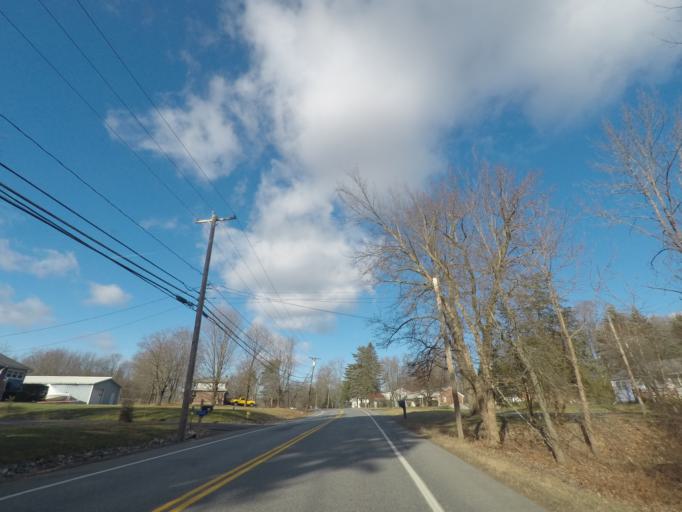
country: US
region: New York
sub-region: Saratoga County
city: Waterford
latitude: 42.8340
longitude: -73.7281
